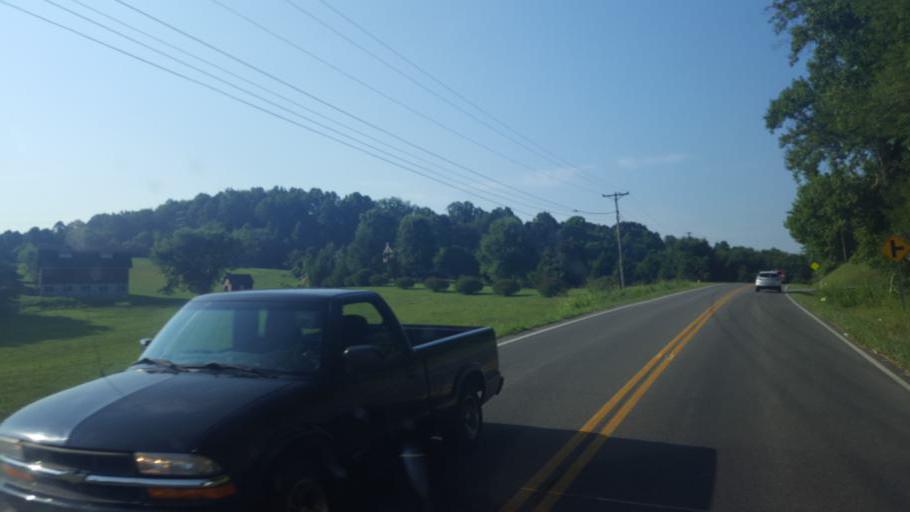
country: US
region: Tennessee
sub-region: Sullivan County
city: Bluff City
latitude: 36.4952
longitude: -82.2617
